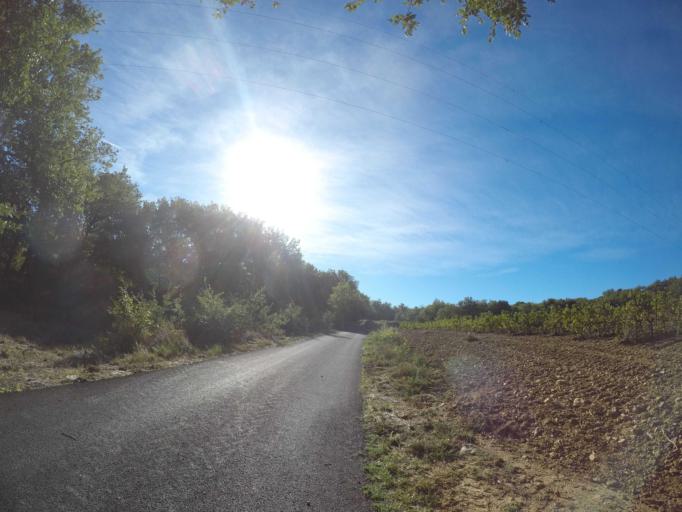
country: FR
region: Languedoc-Roussillon
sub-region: Departement des Pyrenees-Orientales
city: Trouillas
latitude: 42.5713
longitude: 2.7912
